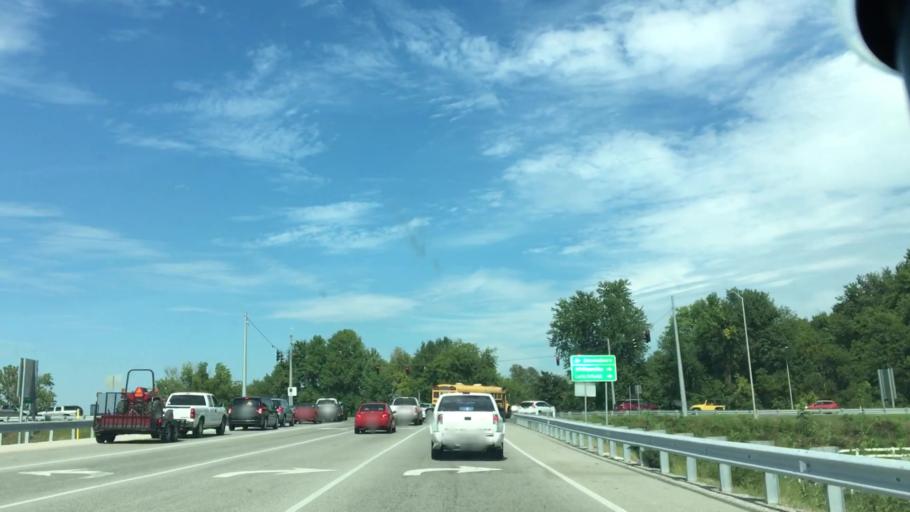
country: US
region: Kentucky
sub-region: Daviess County
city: Owensboro
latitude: 37.7566
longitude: -87.0706
